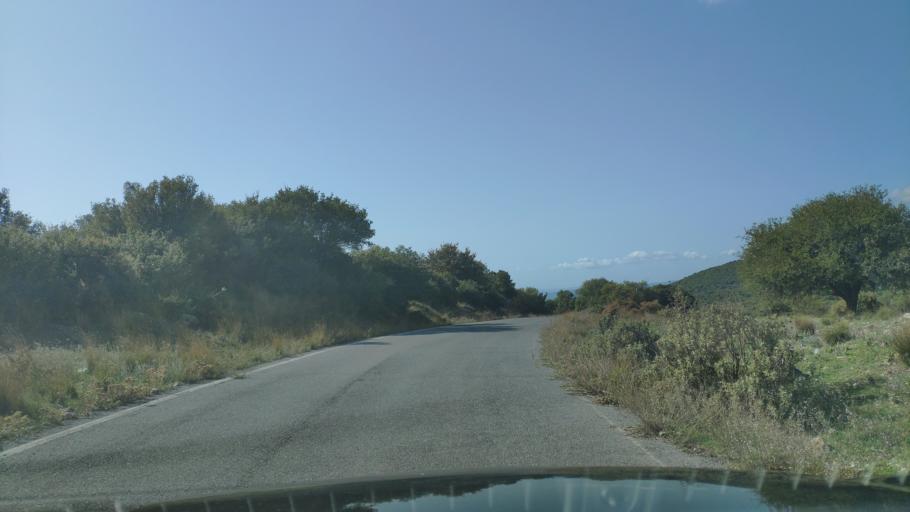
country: GR
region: Peloponnese
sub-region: Nomos Arkadias
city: Dimitsana
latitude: 37.5637
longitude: 22.0007
